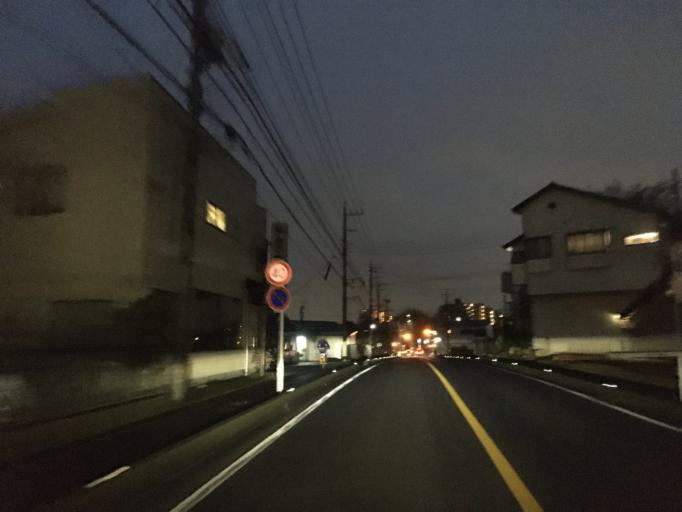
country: JP
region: Saitama
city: Oi
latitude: 35.7983
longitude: 139.5250
